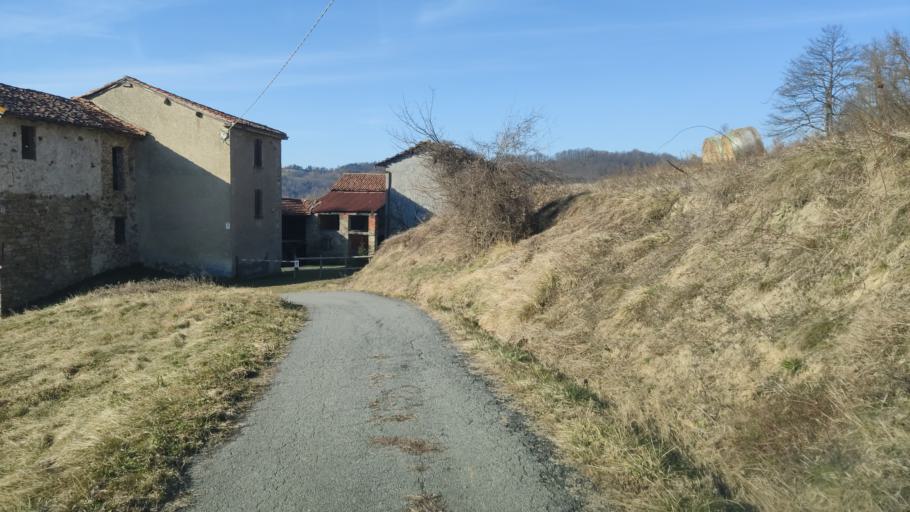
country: IT
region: Piedmont
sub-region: Provincia di Cuneo
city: Camerana
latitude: 44.4126
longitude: 8.1286
